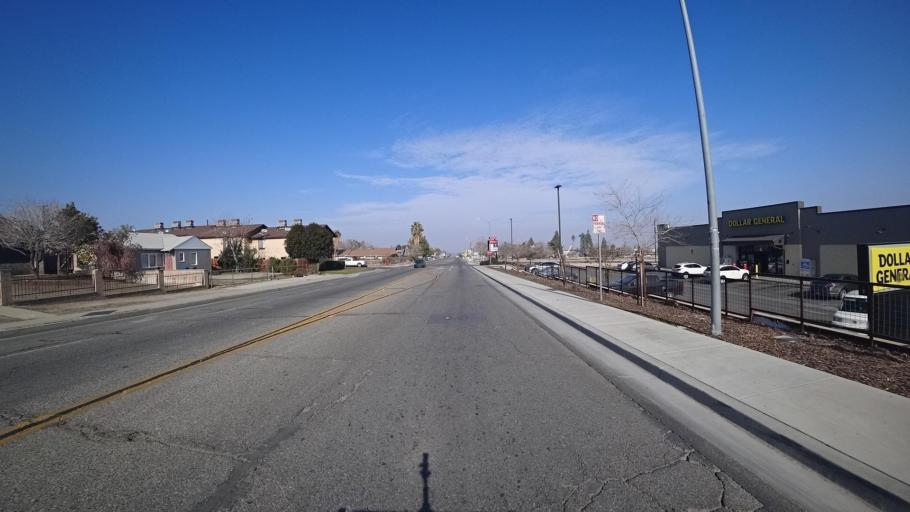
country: US
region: California
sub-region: Kern County
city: Taft
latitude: 35.1395
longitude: -119.4650
